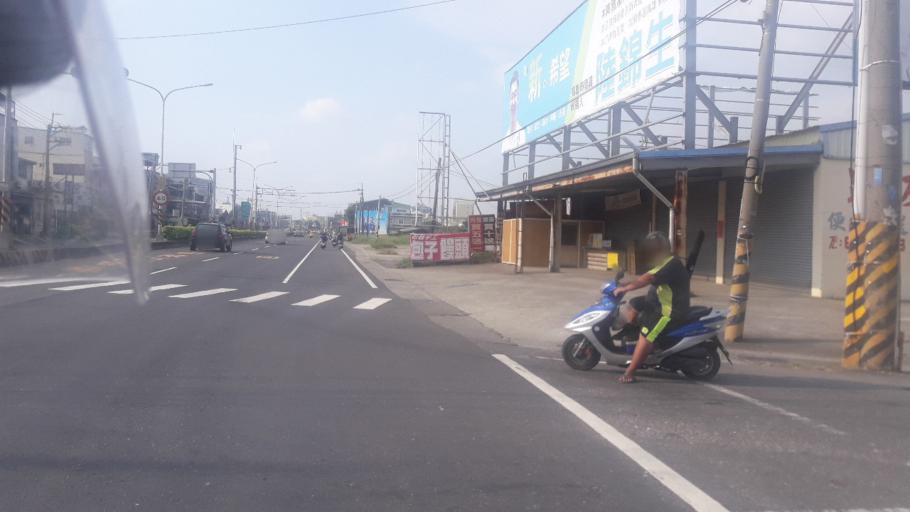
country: TW
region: Taiwan
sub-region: Tainan
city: Tainan
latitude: 22.8737
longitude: 120.2541
